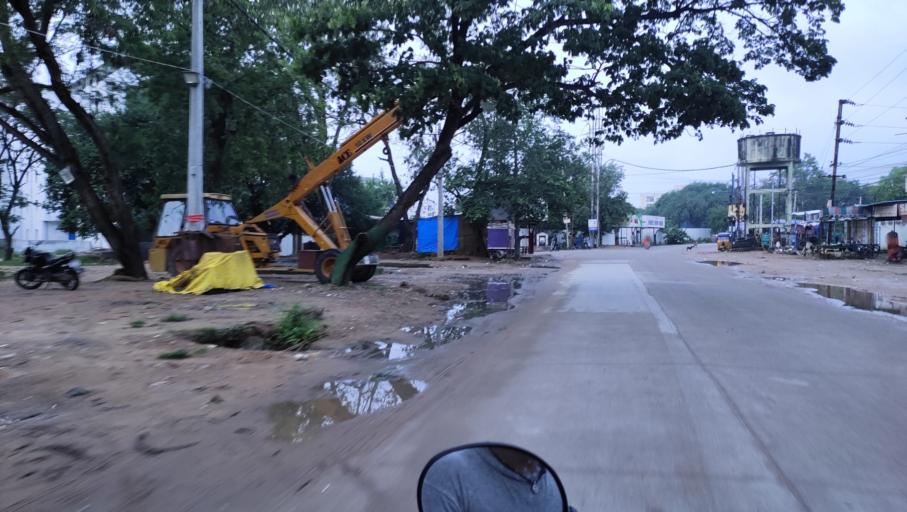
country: IN
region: Telangana
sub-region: Hyderabad
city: Hyderabad
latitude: 17.4007
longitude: 78.3717
